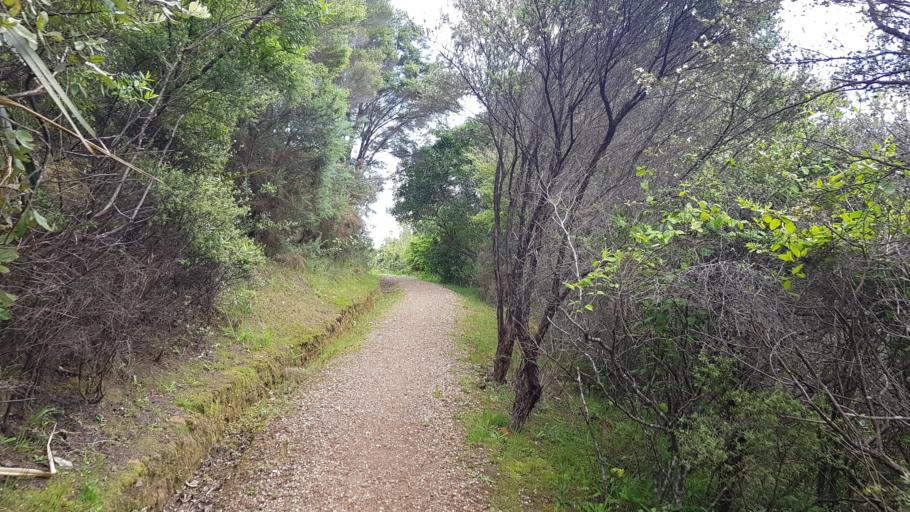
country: NZ
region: Auckland
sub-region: Auckland
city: Pakuranga
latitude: -36.7758
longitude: 175.0049
